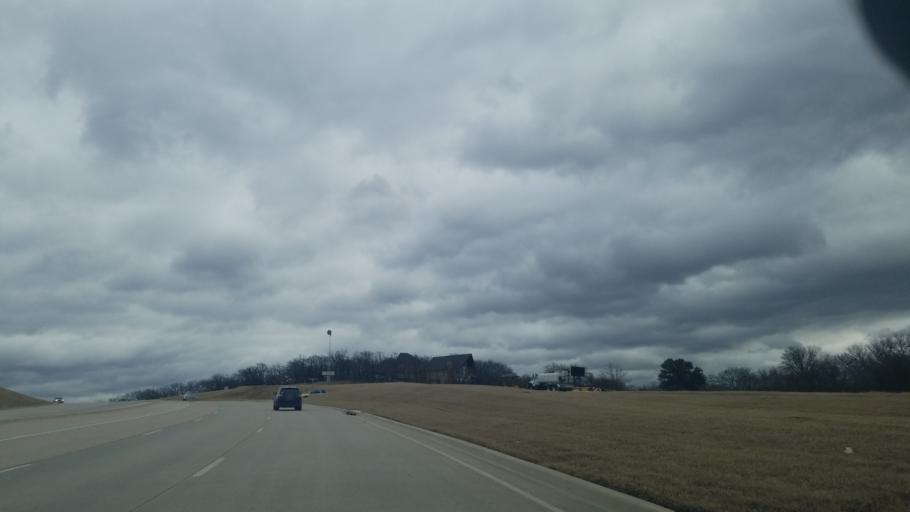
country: US
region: Texas
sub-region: Denton County
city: Trophy Club
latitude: 33.0466
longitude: -97.1770
